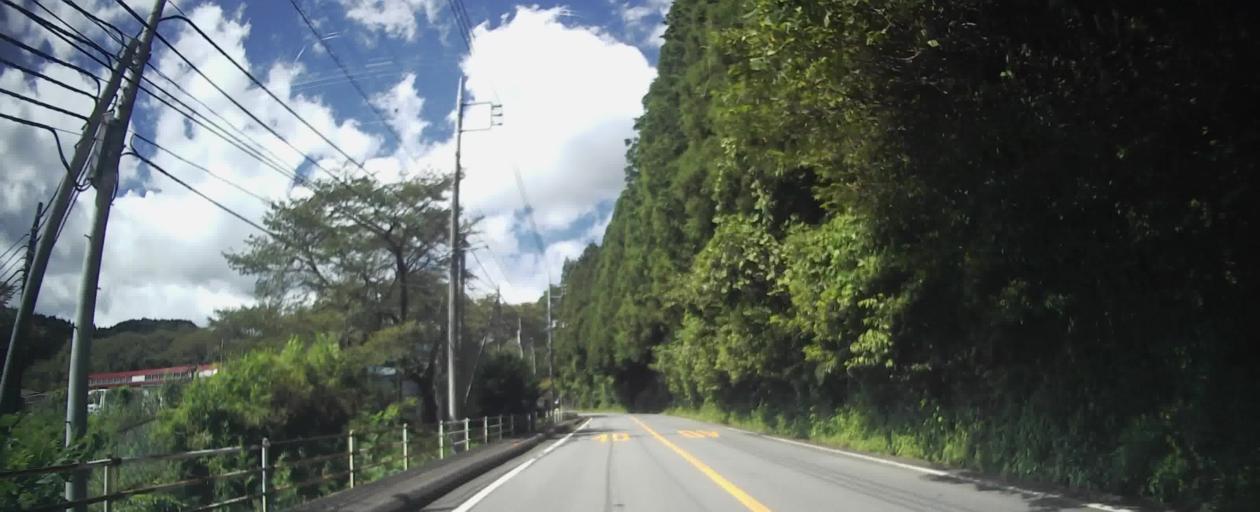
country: JP
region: Gunma
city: Kanekomachi
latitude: 36.4359
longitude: 138.9187
